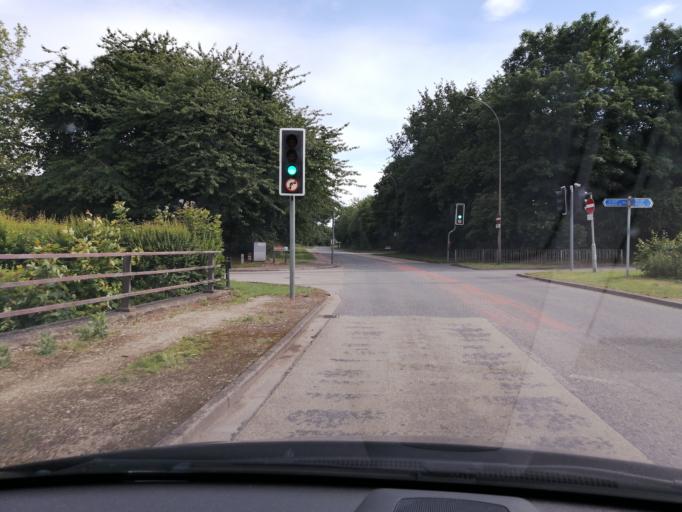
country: GB
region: England
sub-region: Cambridgeshire
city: Yaxley
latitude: 52.5476
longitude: -0.2763
